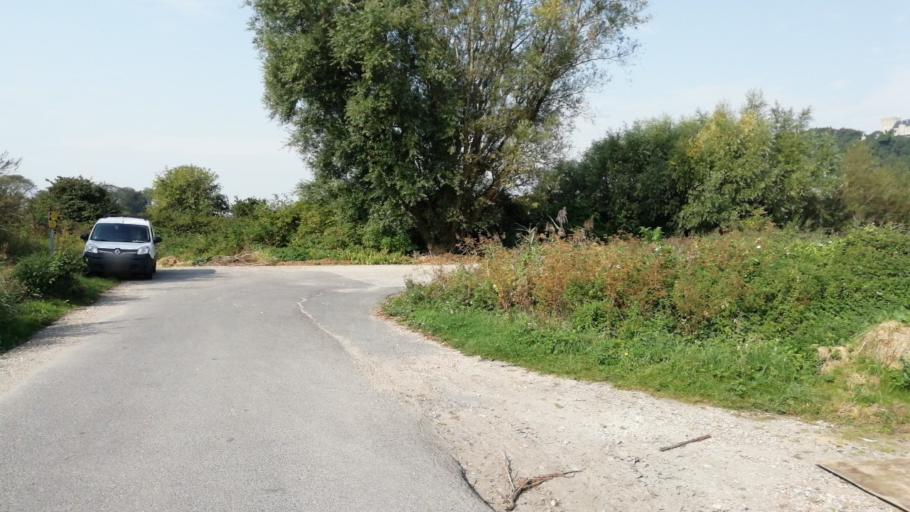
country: FR
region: Haute-Normandie
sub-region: Departement de la Seine-Maritime
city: Rogerville
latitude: 49.4924
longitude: 0.2531
